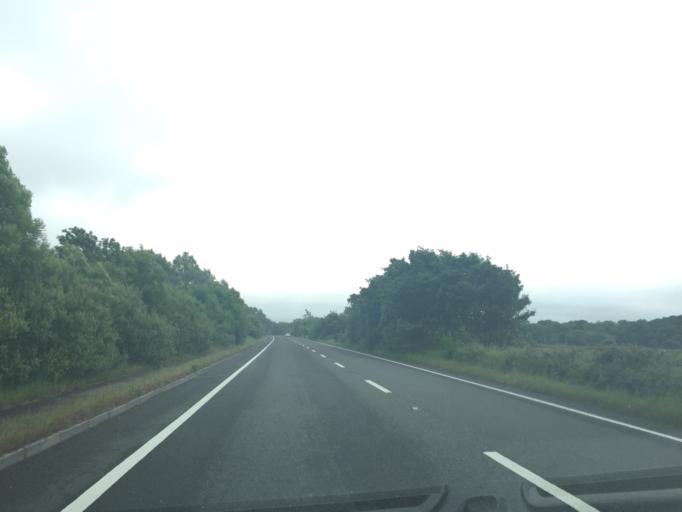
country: GB
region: England
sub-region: Dorset
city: Wareham
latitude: 50.6783
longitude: -2.1207
